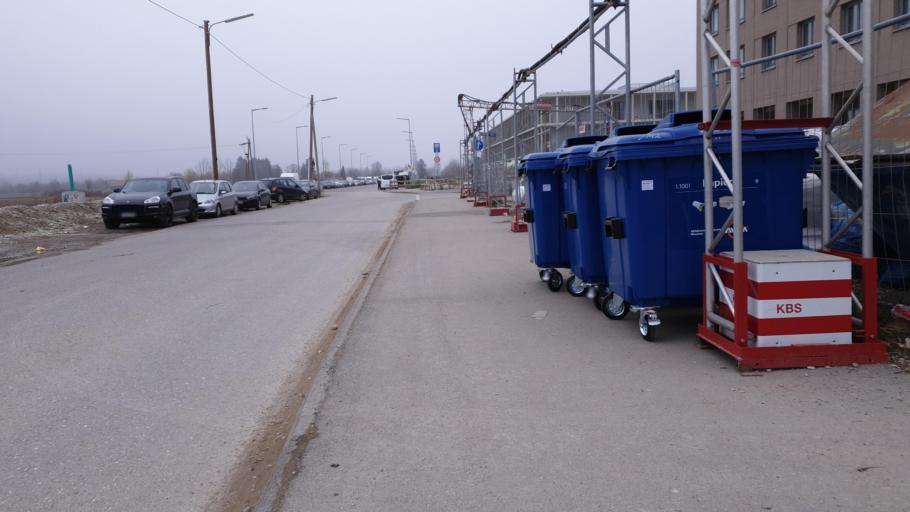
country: DE
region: Bavaria
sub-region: Upper Bavaria
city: Germering
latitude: 48.1516
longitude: 11.4061
